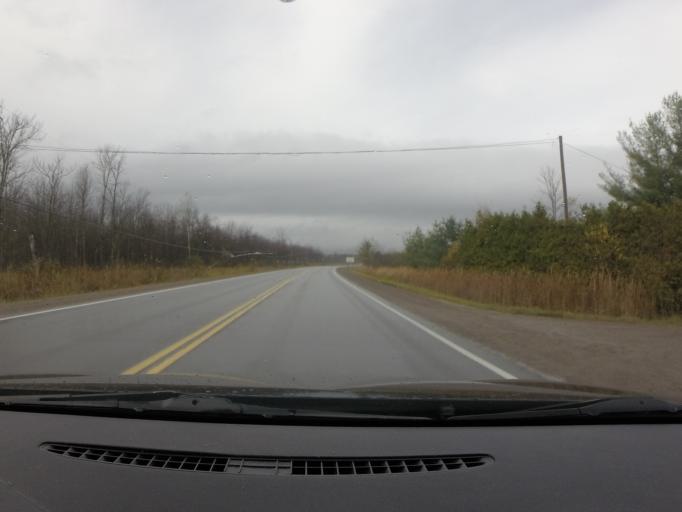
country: CA
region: Ontario
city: Belleville
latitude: 44.5567
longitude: -77.2807
